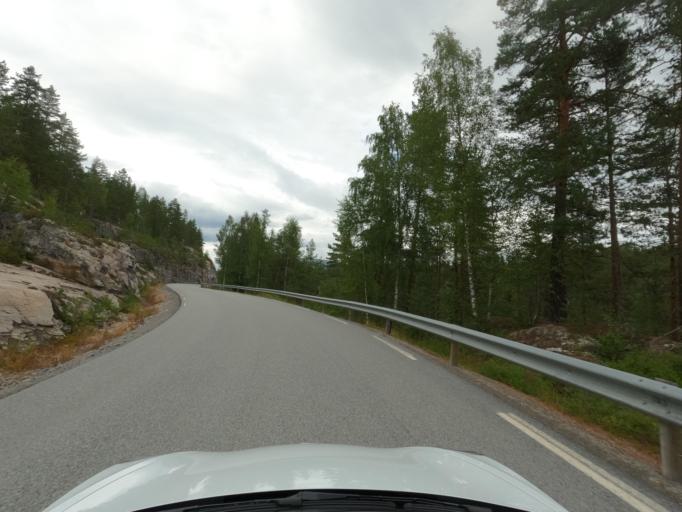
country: NO
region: Telemark
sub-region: Notodden
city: Notodden
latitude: 59.7041
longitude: 9.1515
